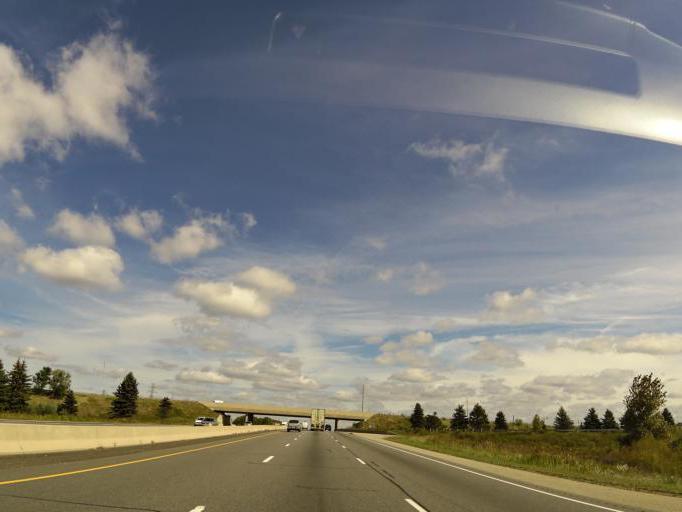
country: CA
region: Ontario
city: London
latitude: 42.9360
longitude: -81.1814
